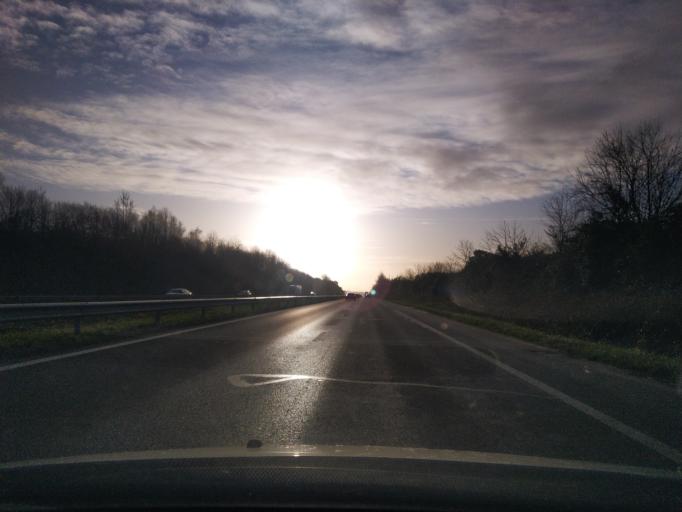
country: FR
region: Haute-Normandie
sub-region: Departement de la Seine-Maritime
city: Maromme
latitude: 49.4774
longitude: 1.0180
